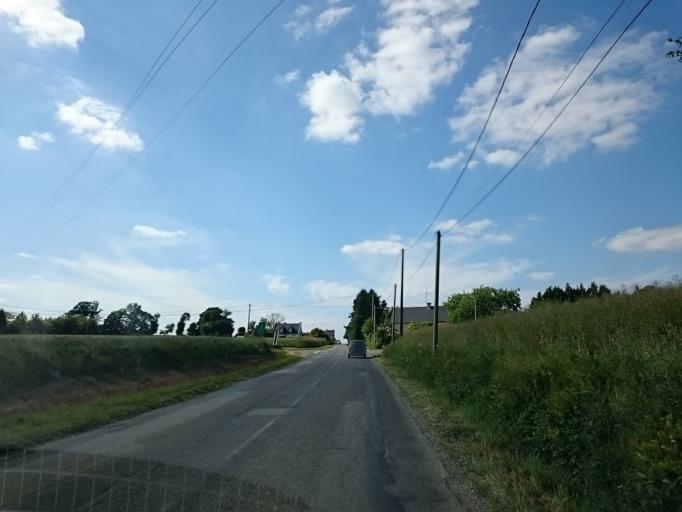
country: FR
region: Brittany
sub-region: Departement d'Ille-et-Vilaine
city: Bourgbarre
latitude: 47.9809
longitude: -1.6136
